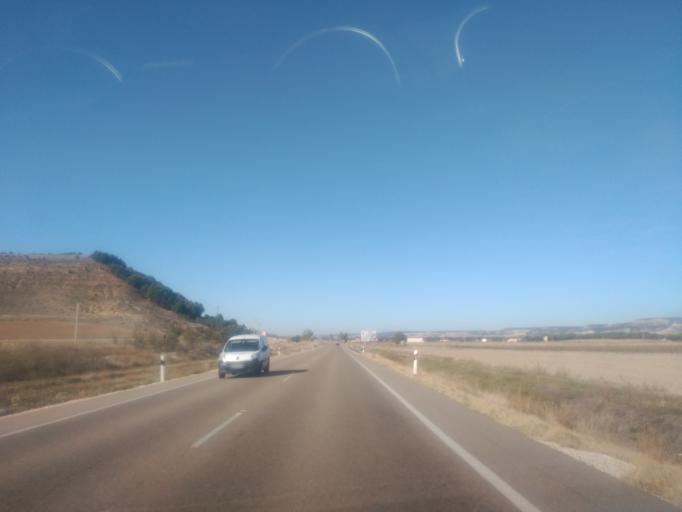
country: ES
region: Castille and Leon
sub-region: Provincia de Valladolid
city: Quintanilla de Arriba
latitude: 41.6165
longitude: -4.1971
